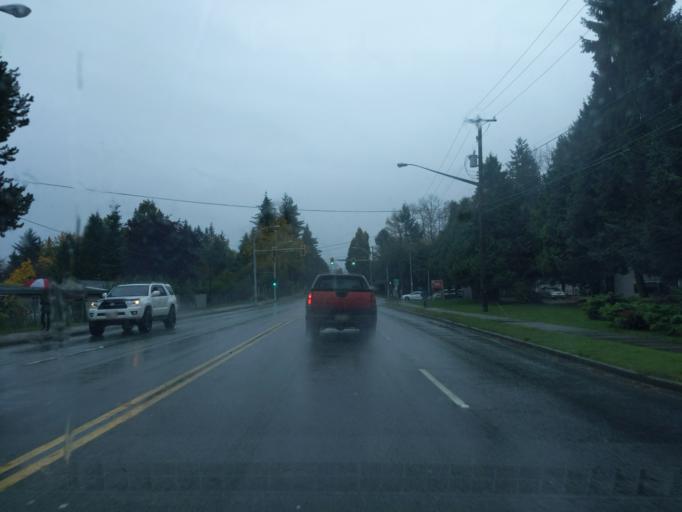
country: CA
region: British Columbia
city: Surrey
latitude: 49.1987
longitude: -122.8073
